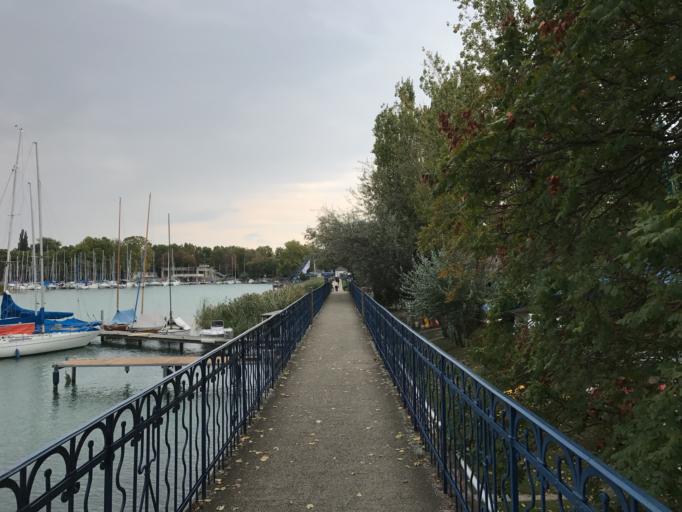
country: HU
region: Somogy
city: Balatonfoldvar
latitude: 46.8572
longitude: 17.8790
